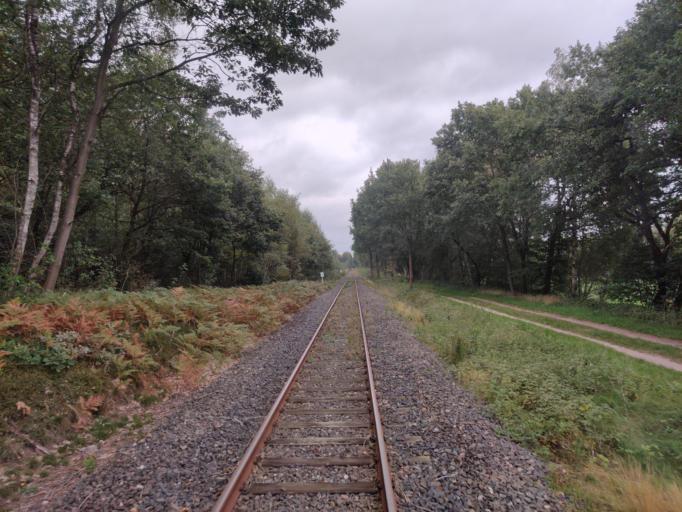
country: DE
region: Lower Saxony
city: Gnarrenburg
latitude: 53.3977
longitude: 9.0138
